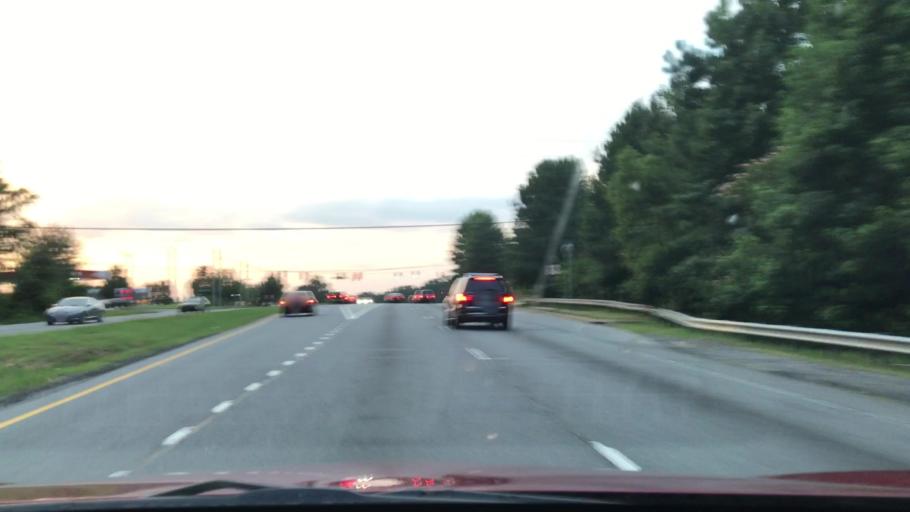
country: US
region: Georgia
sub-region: Gwinnett County
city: Lawrenceville
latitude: 34.0346
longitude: -83.9875
